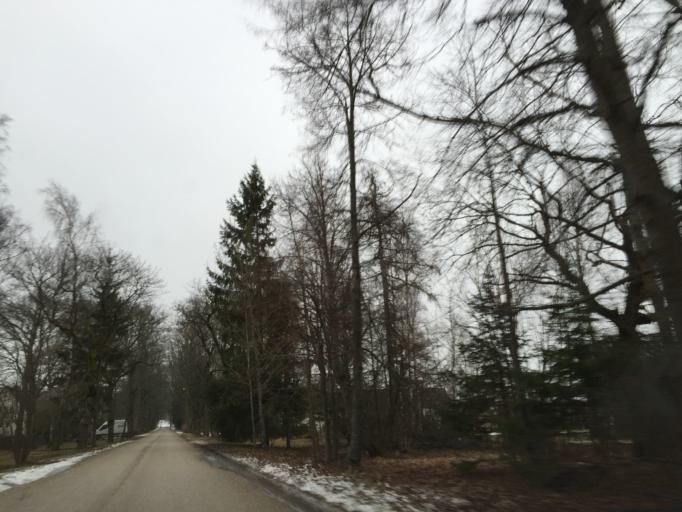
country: EE
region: Laeaene
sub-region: Lihula vald
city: Lihula
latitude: 58.5845
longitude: 23.5372
